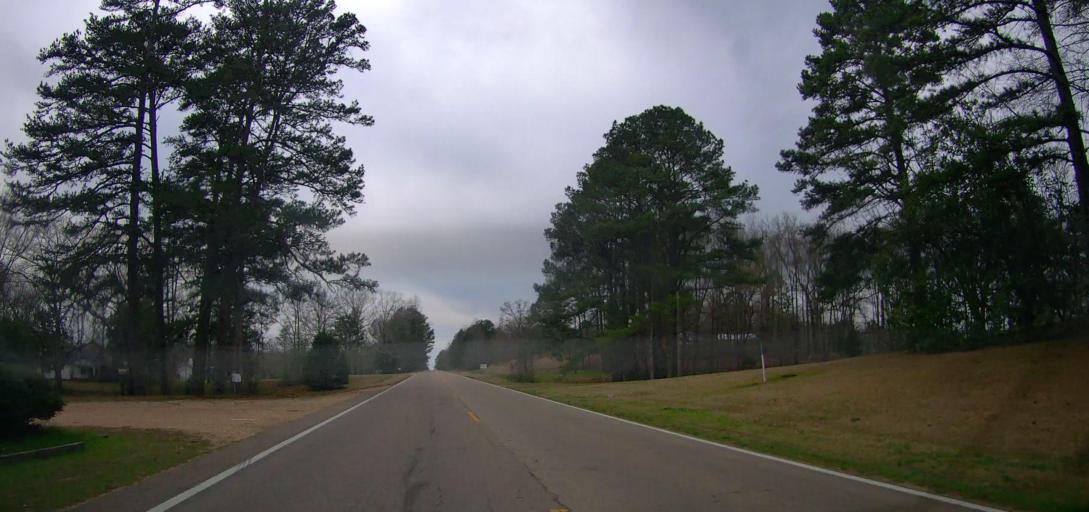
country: US
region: Mississippi
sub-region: Itawamba County
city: Mantachie
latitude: 34.2566
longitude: -88.4990
